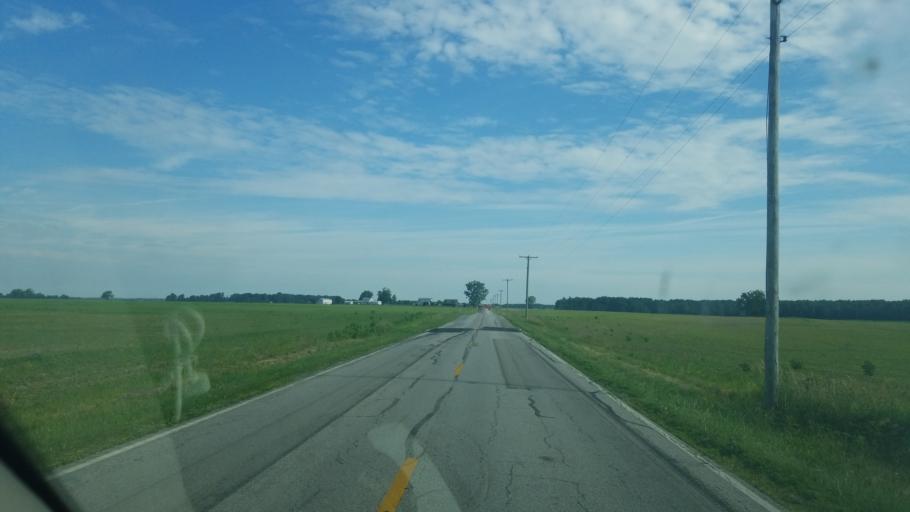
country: US
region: Ohio
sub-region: Marion County
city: Marion
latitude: 40.6666
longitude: -83.2290
